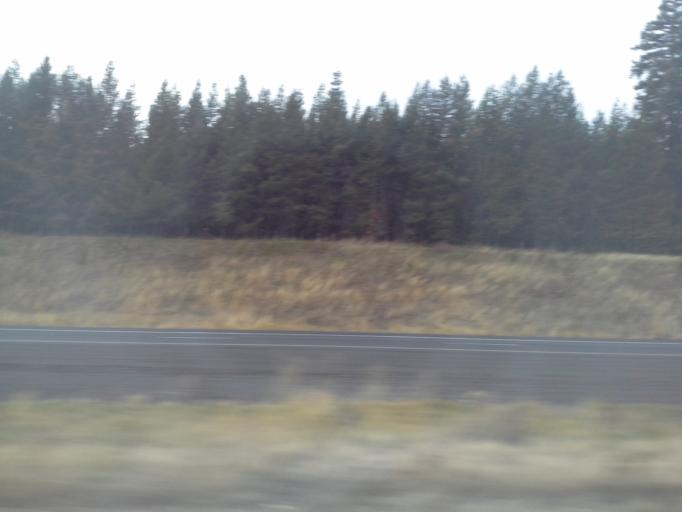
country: US
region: Oregon
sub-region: Umatilla County
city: Mission
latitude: 45.4984
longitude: -118.4184
